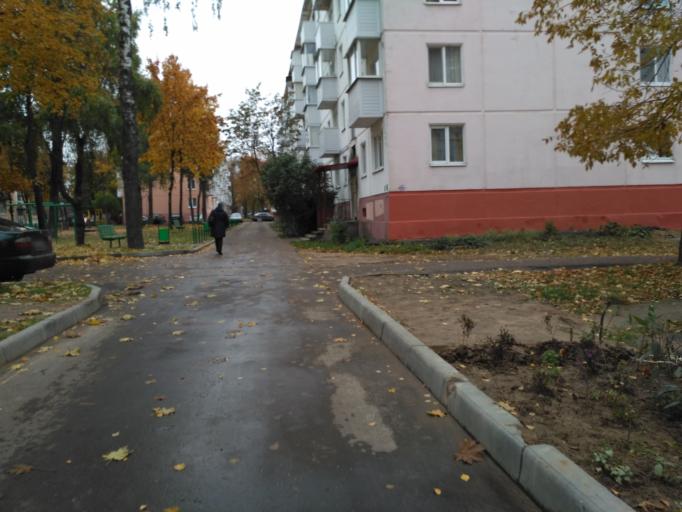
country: BY
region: Minsk
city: Horad Barysaw
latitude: 54.2170
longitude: 28.5062
